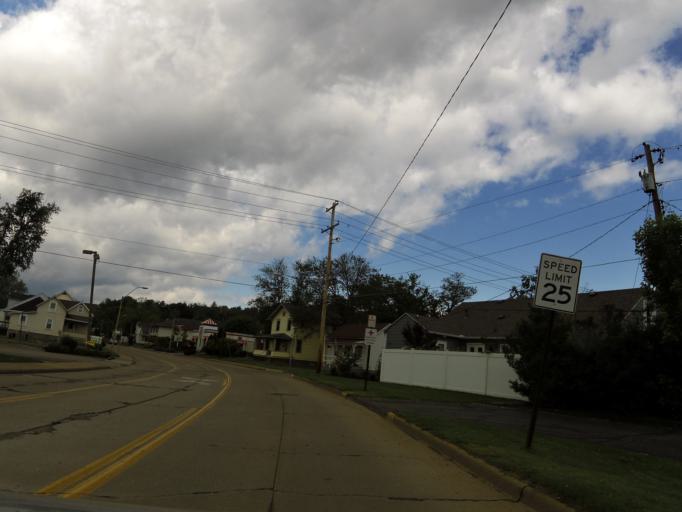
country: US
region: Ohio
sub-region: Athens County
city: Athens
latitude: 39.3321
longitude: -82.0896
